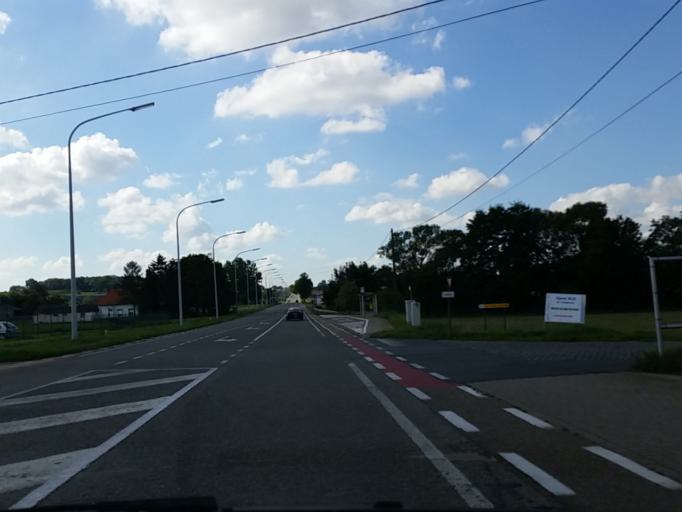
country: BE
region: Flanders
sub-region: Provincie Vlaams-Brabant
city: Bekkevoort
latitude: 50.9331
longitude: 4.9375
